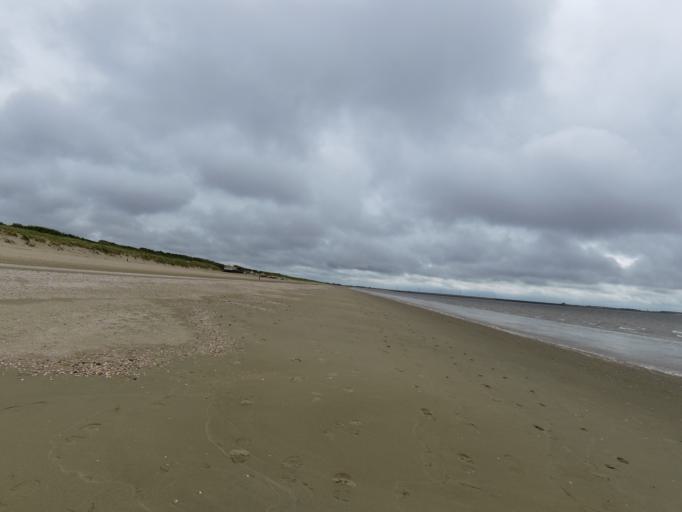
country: NL
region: South Holland
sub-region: Gemeente Goeree-Overflakkee
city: Goedereede
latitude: 51.8722
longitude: 4.0463
